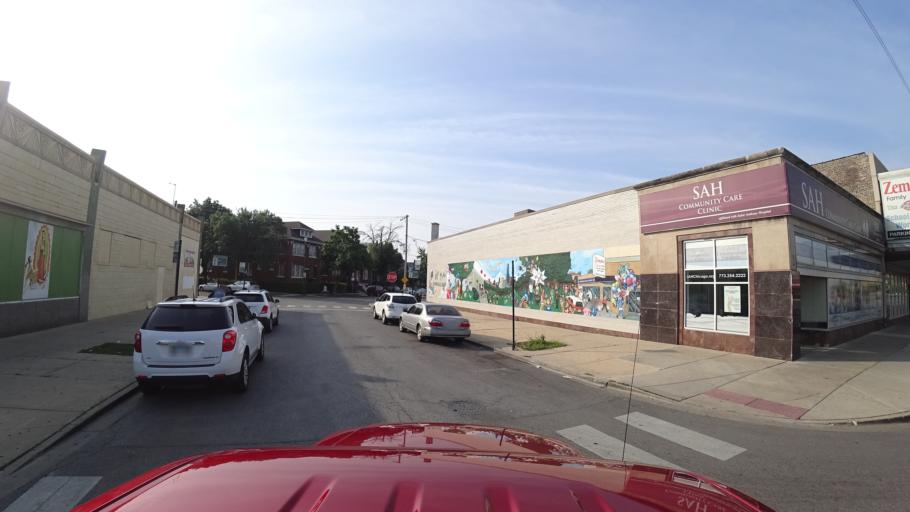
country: US
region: Illinois
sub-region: Cook County
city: Chicago
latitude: 41.8176
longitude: -87.6985
